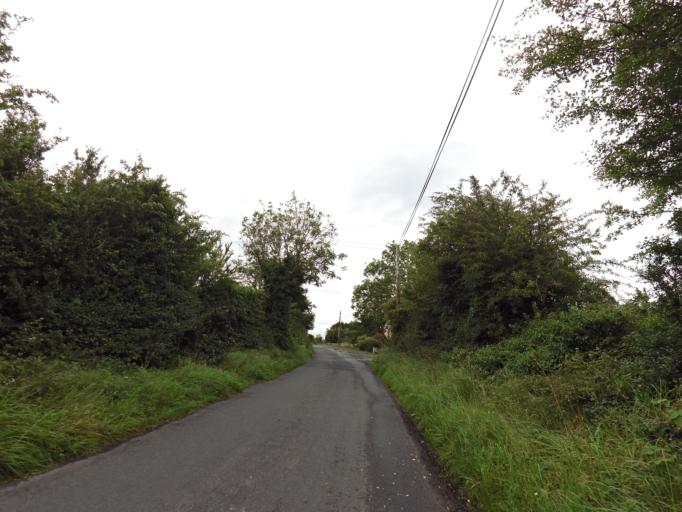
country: IE
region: Connaught
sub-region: County Galway
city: Gaillimh
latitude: 53.3080
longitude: -9.0684
